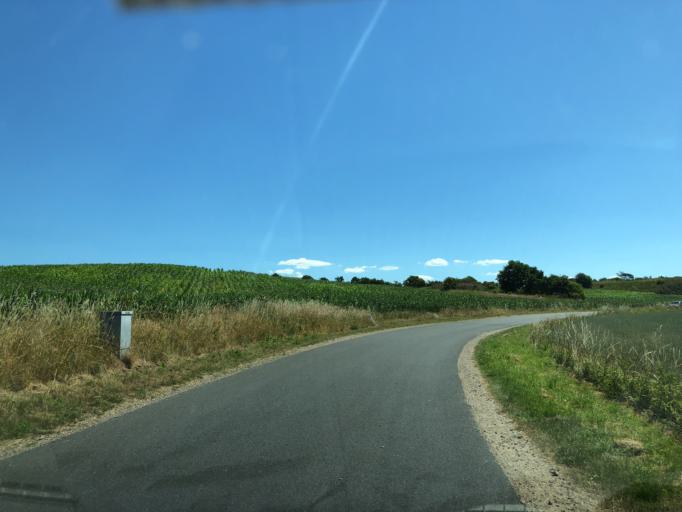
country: DK
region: Central Jutland
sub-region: Viborg Kommune
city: Viborg
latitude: 56.5411
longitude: 9.4664
